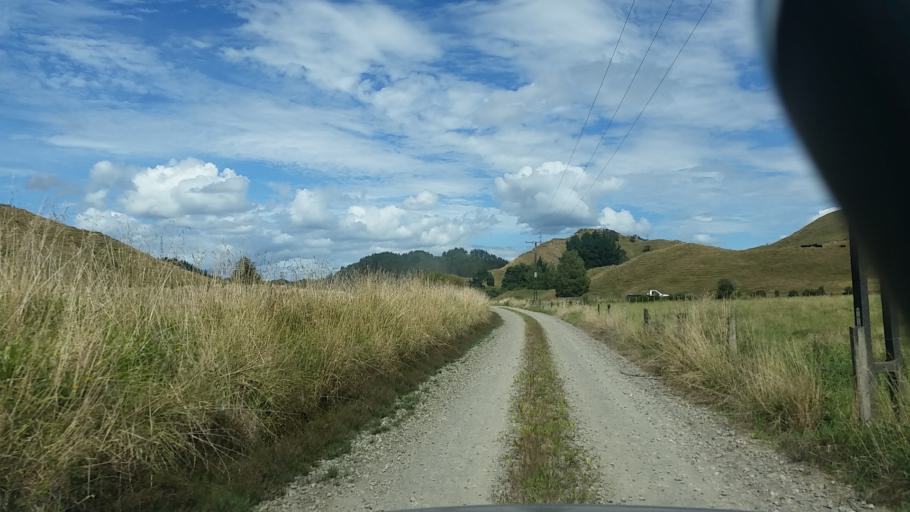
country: NZ
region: Taranaki
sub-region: South Taranaki District
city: Eltham
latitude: -39.2243
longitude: 174.5629
